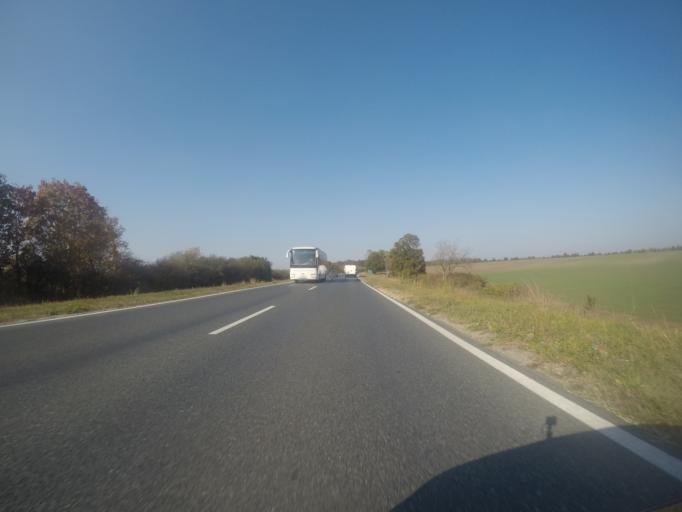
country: HU
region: Tolna
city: Bolcske
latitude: 46.7300
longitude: 18.8827
